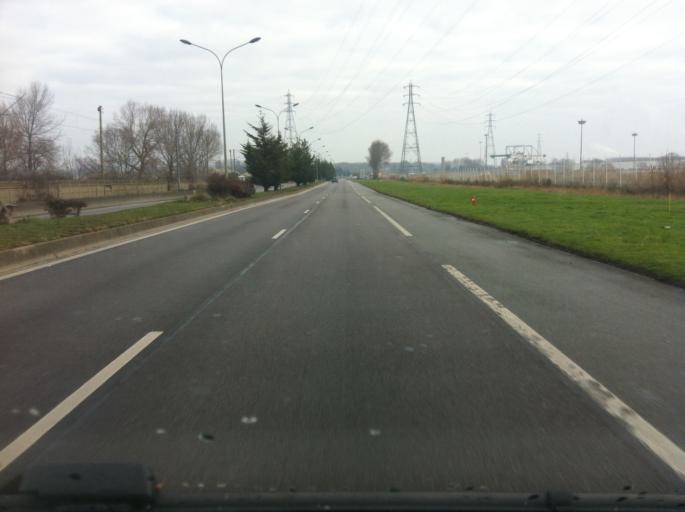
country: FR
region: Haute-Normandie
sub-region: Departement de la Seine-Maritime
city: Harfleur
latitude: 49.4849
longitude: 0.1739
